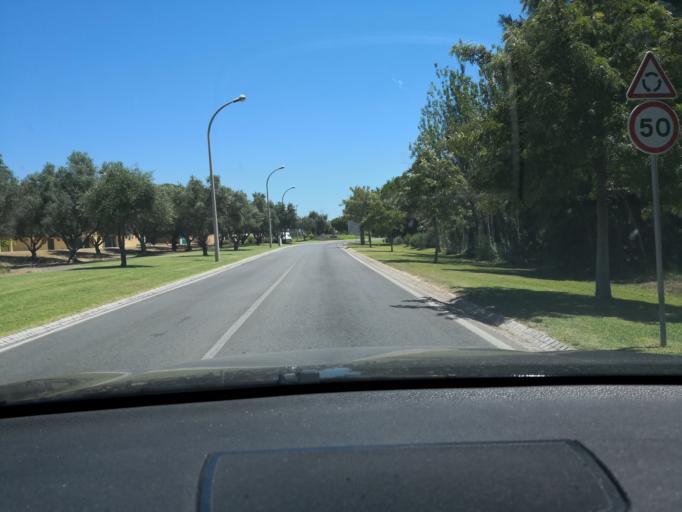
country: PT
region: Faro
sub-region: Loule
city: Vilamoura
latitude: 37.1053
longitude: -8.1315
